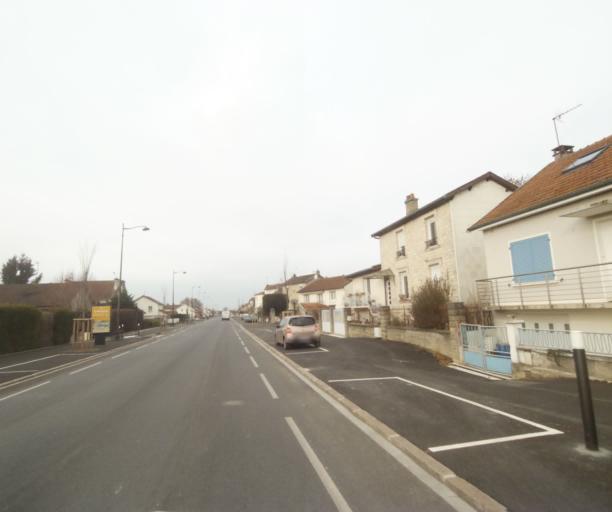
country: FR
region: Champagne-Ardenne
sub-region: Departement de la Haute-Marne
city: Saint-Dizier
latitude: 48.6389
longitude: 4.9248
